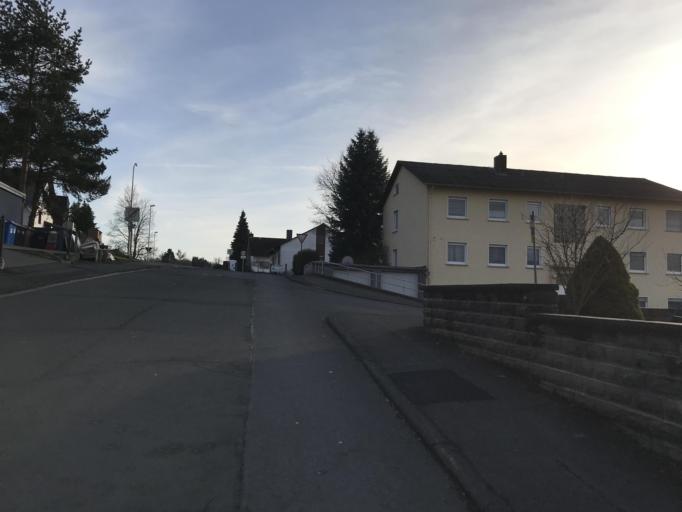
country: DE
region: Hesse
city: Weilburg
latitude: 50.4851
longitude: 8.2760
